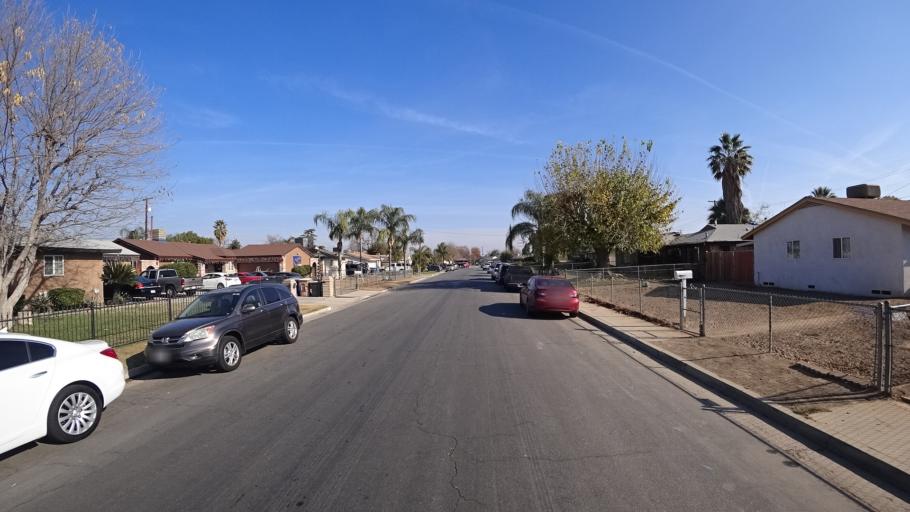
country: US
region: California
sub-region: Kern County
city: Bakersfield
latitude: 35.3258
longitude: -119.0198
